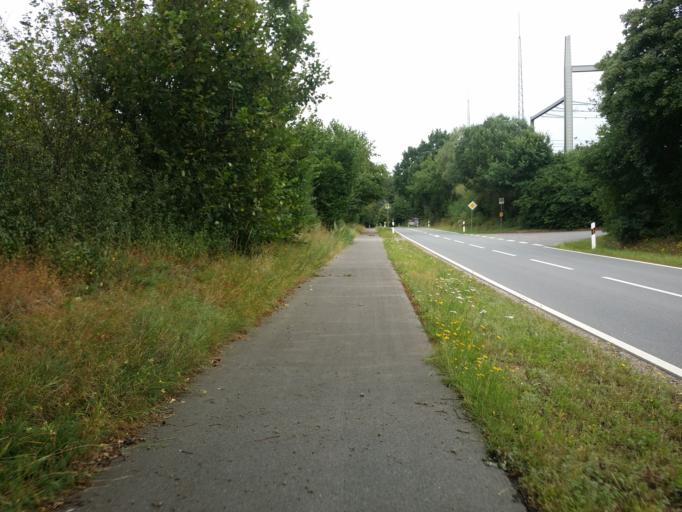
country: DE
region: Schleswig-Holstein
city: Huje
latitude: 53.9665
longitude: 9.4476
